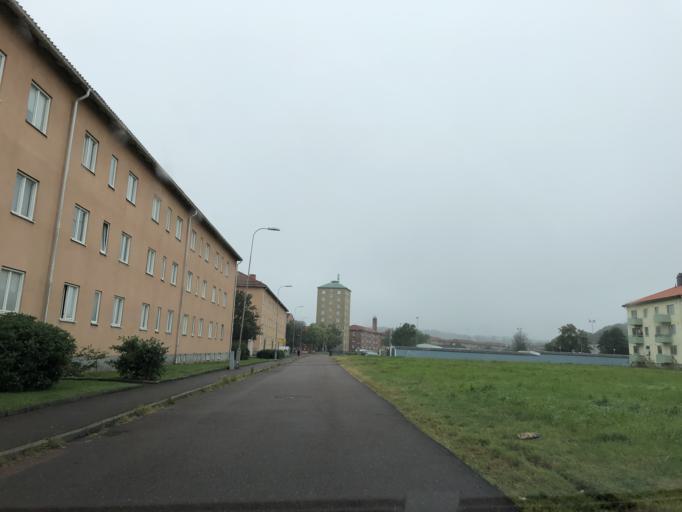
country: SE
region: Vaestra Goetaland
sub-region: Goteborg
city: Majorna
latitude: 57.7295
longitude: 11.9307
